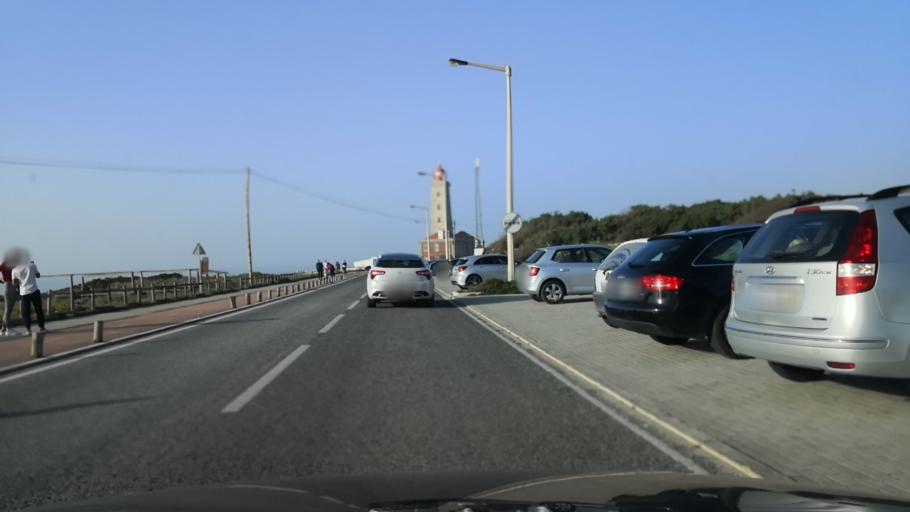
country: PT
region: Leiria
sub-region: Alcobaca
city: Pataias
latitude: 39.7619
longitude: -9.0307
